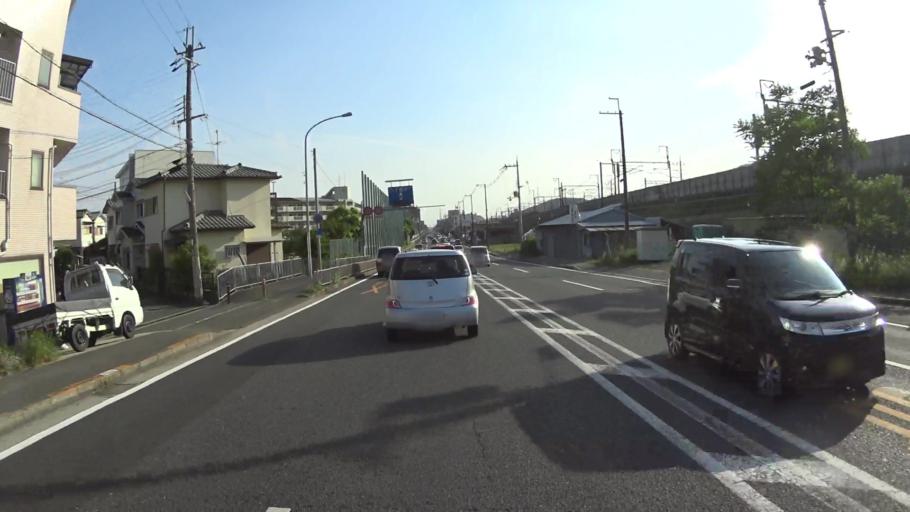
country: JP
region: Kyoto
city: Yawata
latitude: 34.8852
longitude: 135.6759
